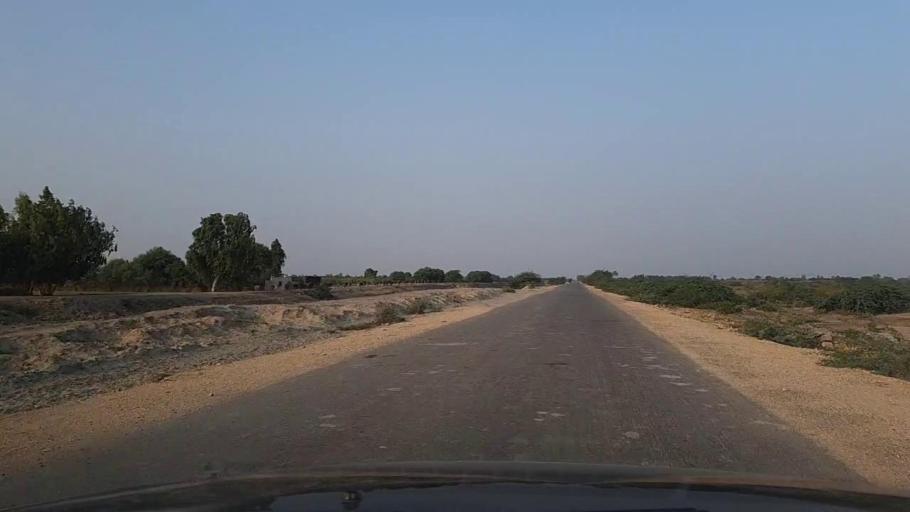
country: PK
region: Sindh
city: Mirpur Sakro
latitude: 24.4883
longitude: 67.8084
